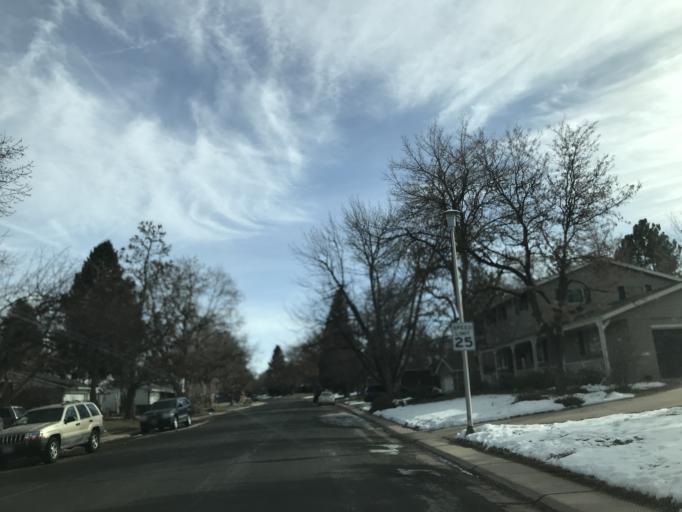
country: US
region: Colorado
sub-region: Arapahoe County
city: Columbine Valley
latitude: 39.5950
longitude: -105.0151
